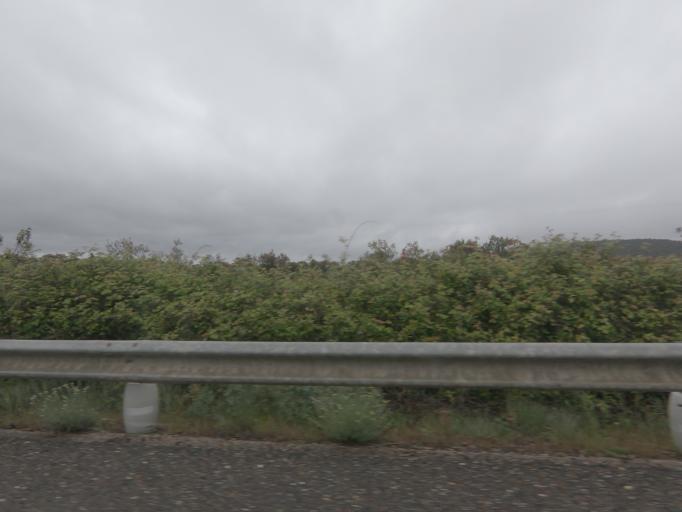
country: ES
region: Extremadura
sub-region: Provincia de Badajoz
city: Puebla de Obando
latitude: 39.1578
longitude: -6.6439
